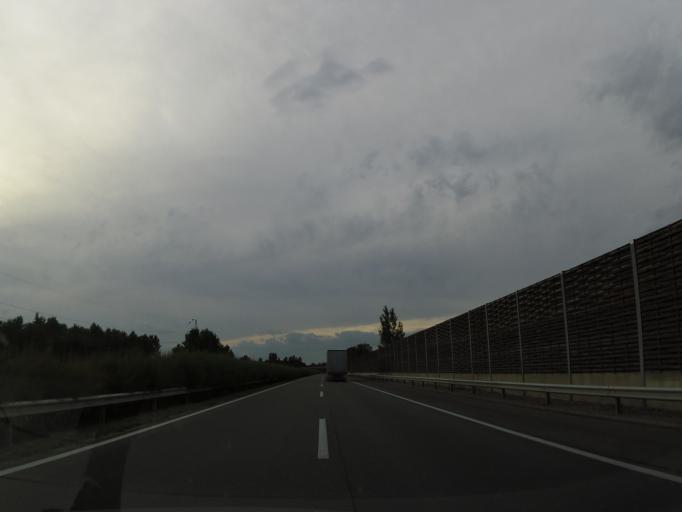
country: HU
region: Pest
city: Hernad
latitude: 47.1672
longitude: 19.4454
